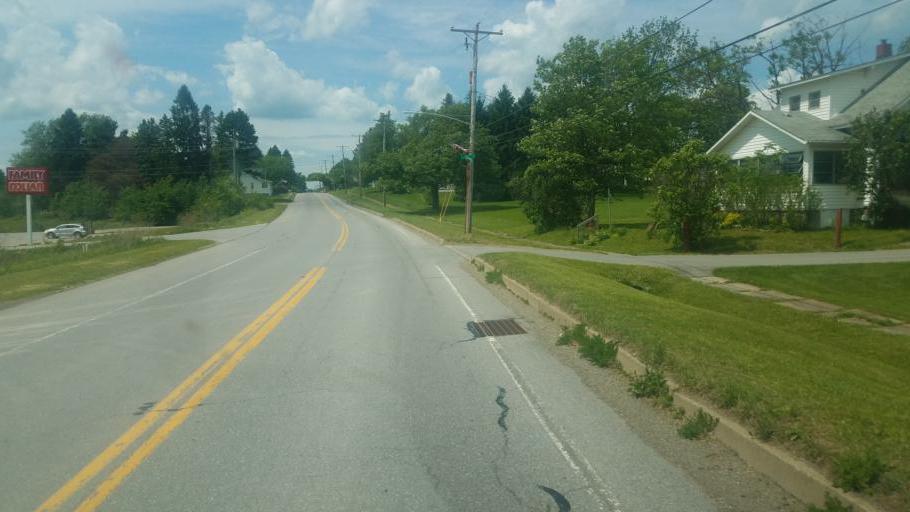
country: US
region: Pennsylvania
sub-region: Venango County
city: Franklin
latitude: 41.1943
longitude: -79.8694
